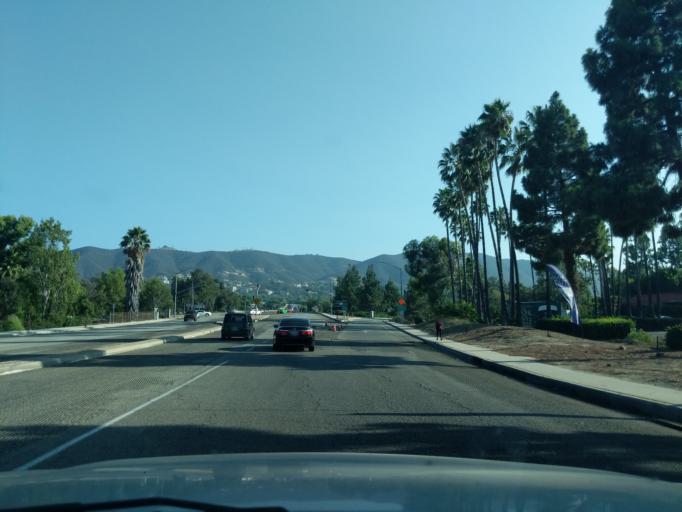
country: US
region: California
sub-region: Ventura County
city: Casa Conejo
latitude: 34.1866
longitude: -118.9113
